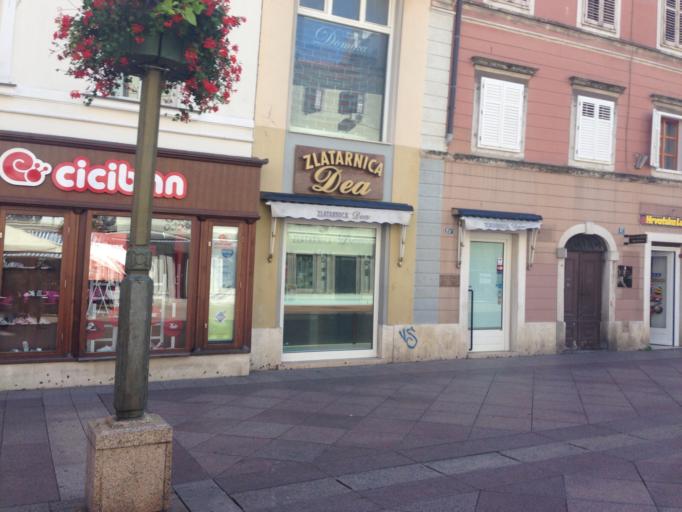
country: HR
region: Primorsko-Goranska
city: Drenova
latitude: 45.3271
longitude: 14.4418
